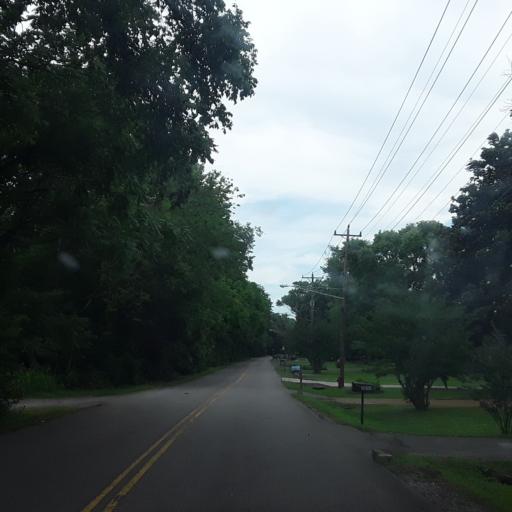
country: US
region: Tennessee
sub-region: Davidson County
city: Oak Hill
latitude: 36.0678
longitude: -86.7685
